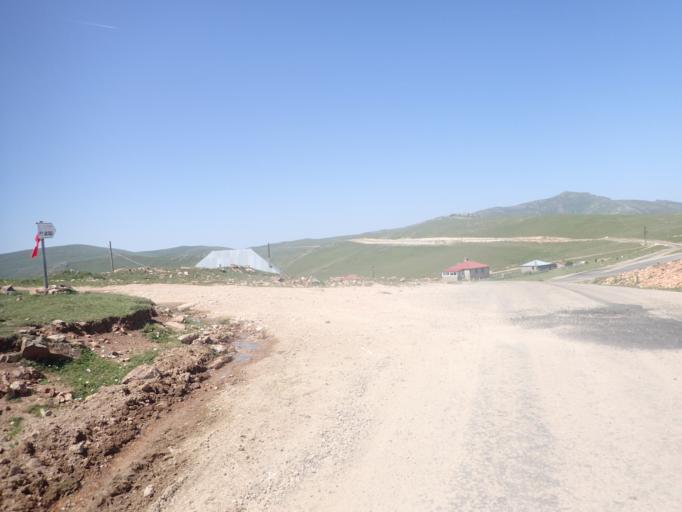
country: TR
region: Ordu
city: Yesilce
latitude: 40.6044
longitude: 37.9129
